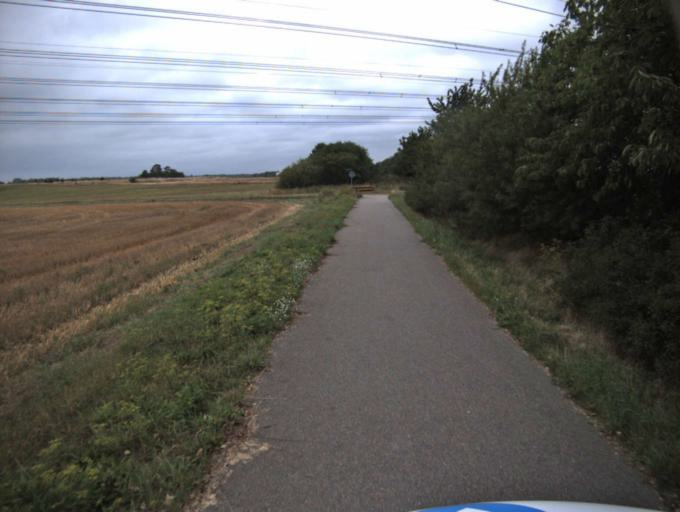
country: SE
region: Skane
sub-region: Kavlinge Kommun
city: Hofterup
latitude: 55.7750
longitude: 12.9867
